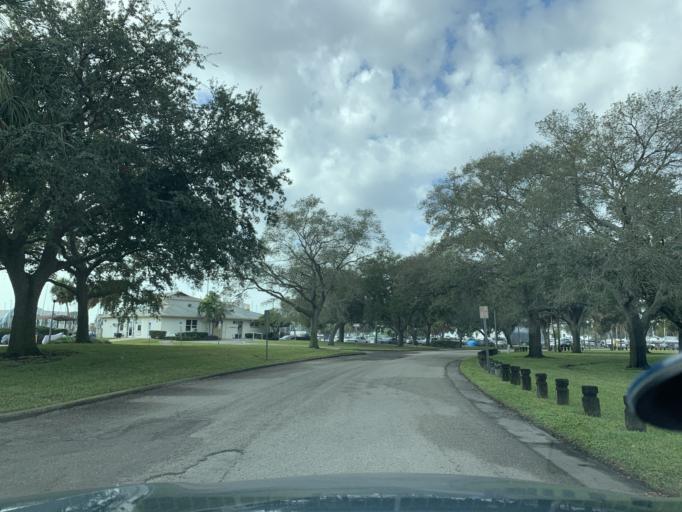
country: US
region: Florida
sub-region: Pinellas County
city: Saint Petersburg
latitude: 27.7701
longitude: -82.6295
